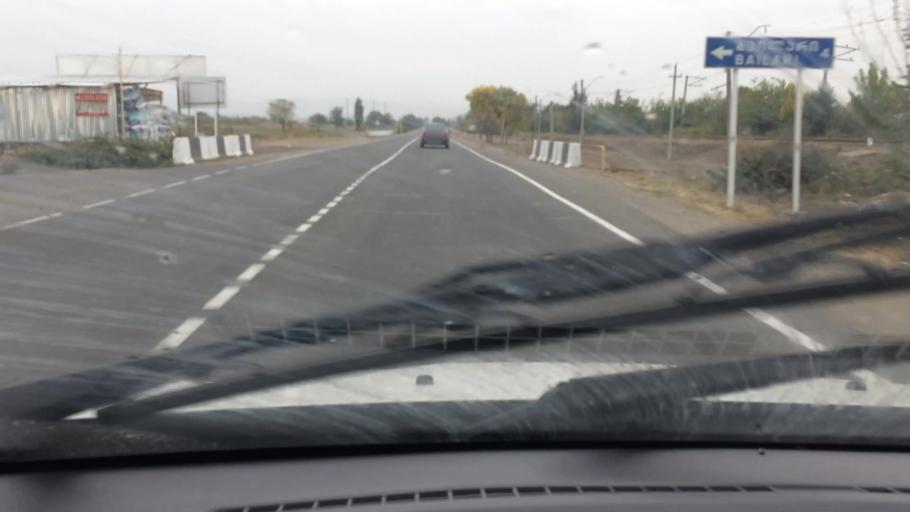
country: GE
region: Kvemo Kartli
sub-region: Marneuli
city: Marneuli
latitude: 41.4220
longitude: 44.8245
